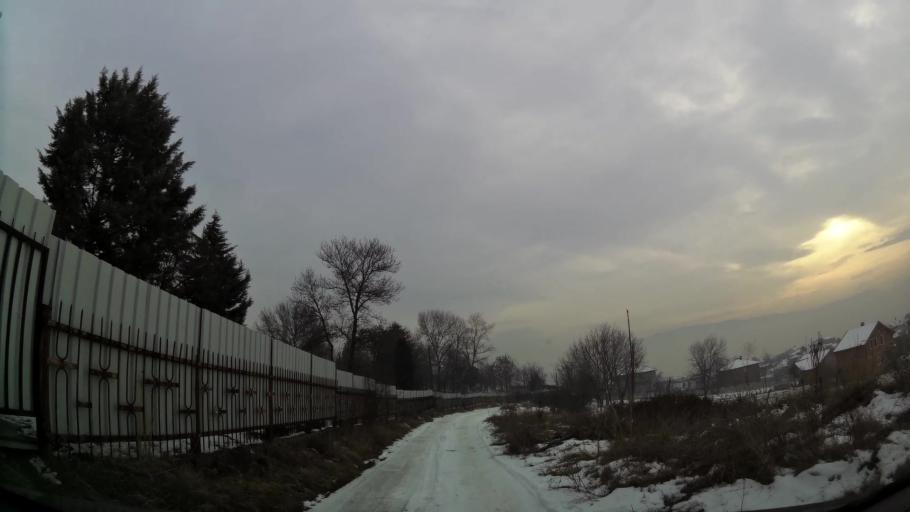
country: MK
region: Suto Orizari
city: Suto Orizare
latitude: 42.0409
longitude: 21.4312
